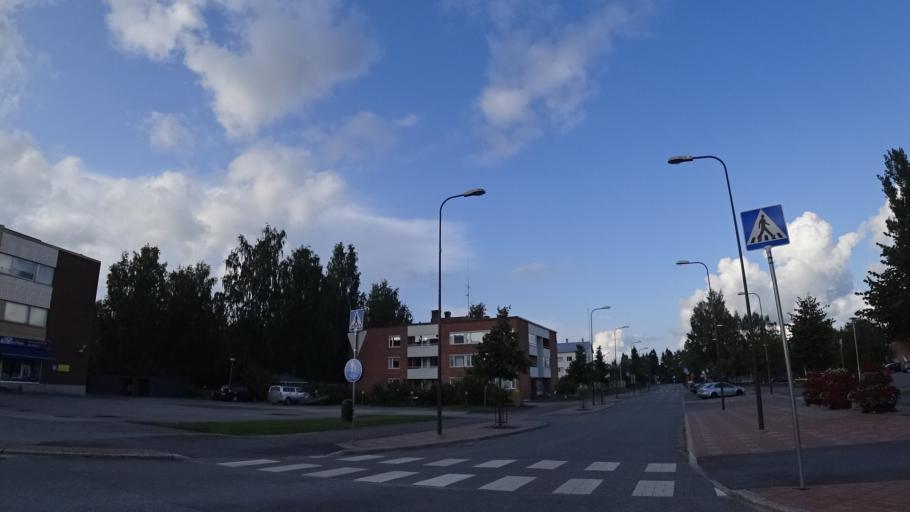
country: FI
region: North Karelia
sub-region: Pielisen Karjala
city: Lieksa
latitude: 63.3185
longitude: 30.0266
